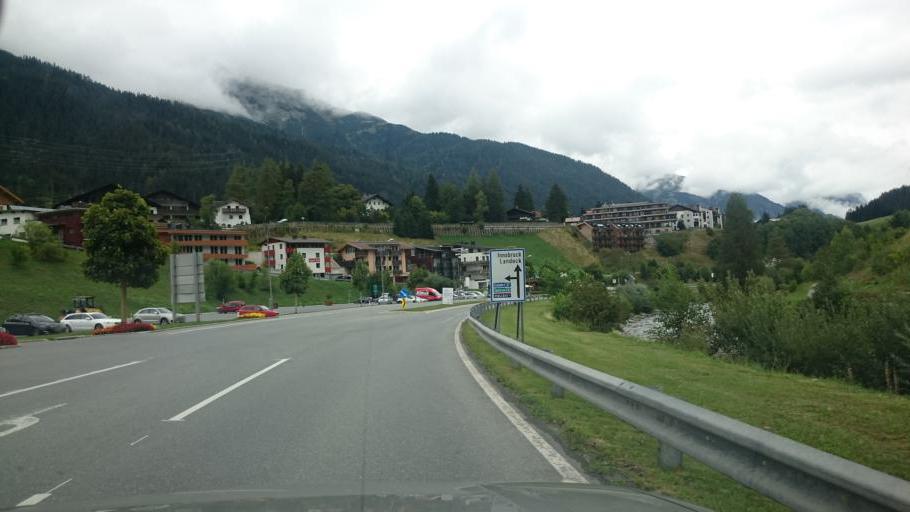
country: AT
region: Tyrol
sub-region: Politischer Bezirk Landeck
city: Sankt Anton am Arlberg
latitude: 47.1347
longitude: 10.2754
